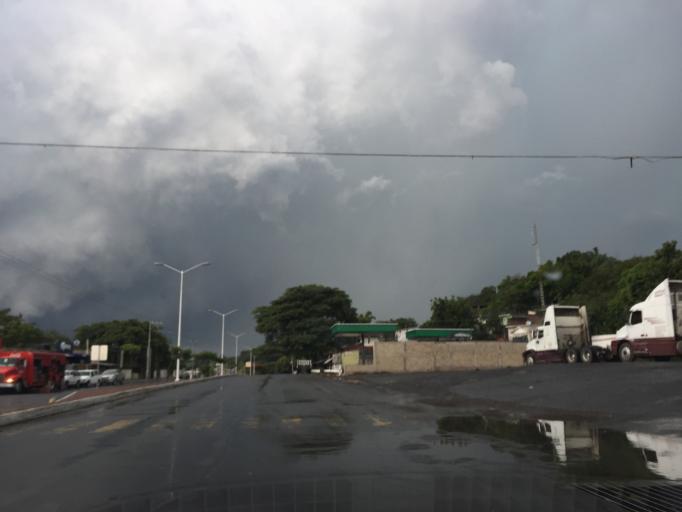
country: MX
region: Colima
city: Queseria
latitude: 19.3861
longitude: -103.5685
